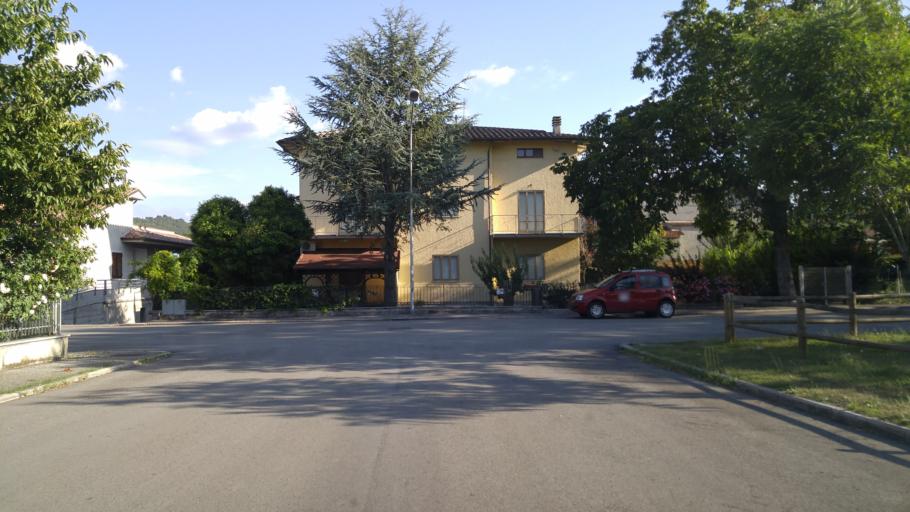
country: IT
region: The Marches
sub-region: Provincia di Pesaro e Urbino
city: Acqualagna
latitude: 43.6140
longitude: 12.6324
